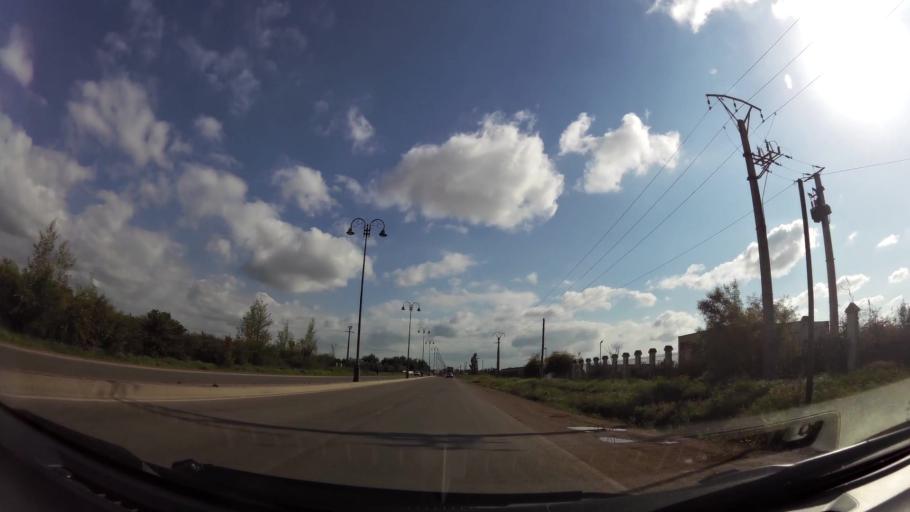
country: MA
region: Chaouia-Ouardigha
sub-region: Settat Province
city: Berrechid
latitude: 33.2935
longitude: -7.5750
